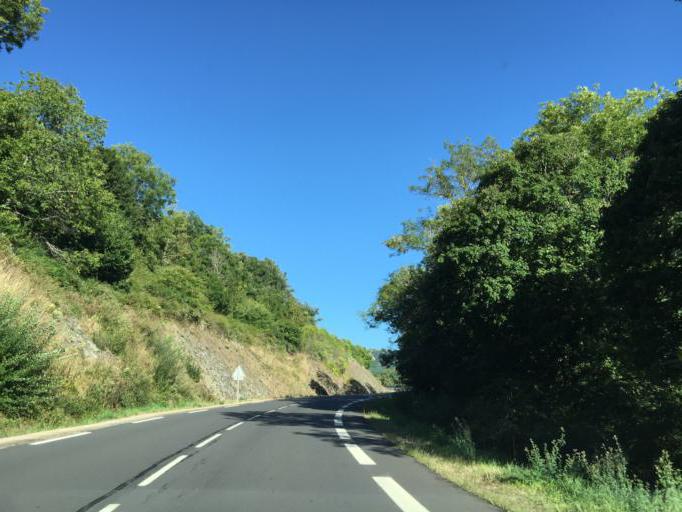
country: FR
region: Auvergne
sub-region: Departement de la Haute-Loire
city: Bains
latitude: 44.9733
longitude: 3.6681
